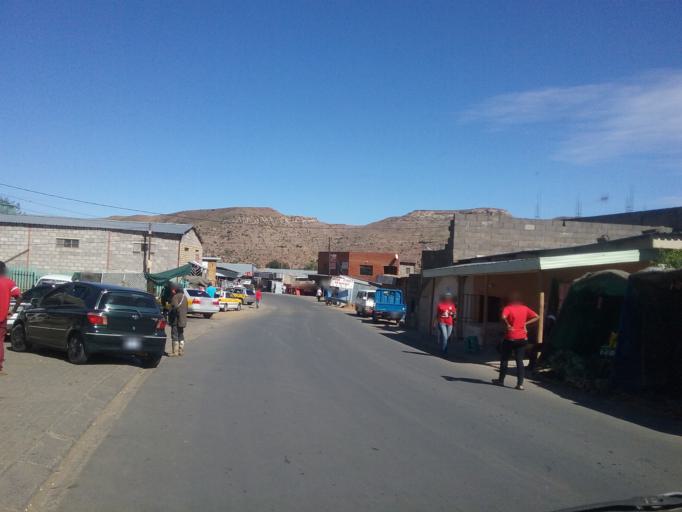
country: LS
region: Quthing
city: Quthing
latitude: -30.4004
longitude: 27.7019
